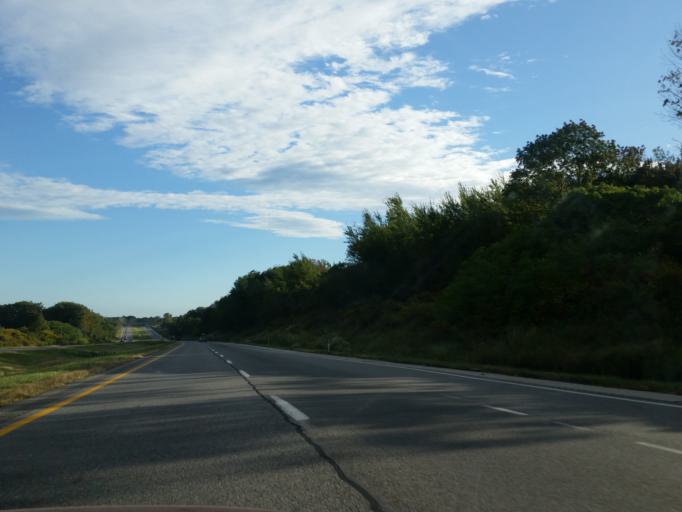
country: US
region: Pennsylvania
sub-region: Erie County
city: North East
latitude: 42.1922
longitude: -79.8244
